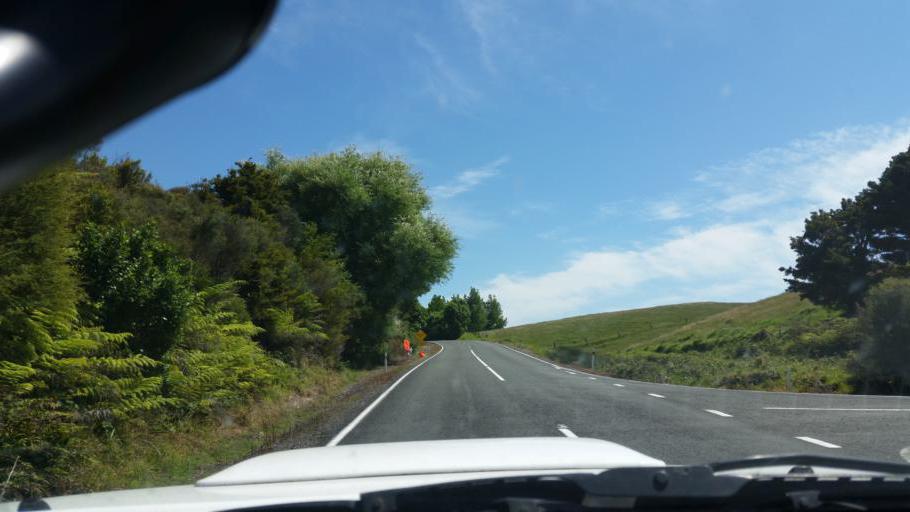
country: NZ
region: Auckland
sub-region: Auckland
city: Wellsford
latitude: -36.1845
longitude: 174.4117
